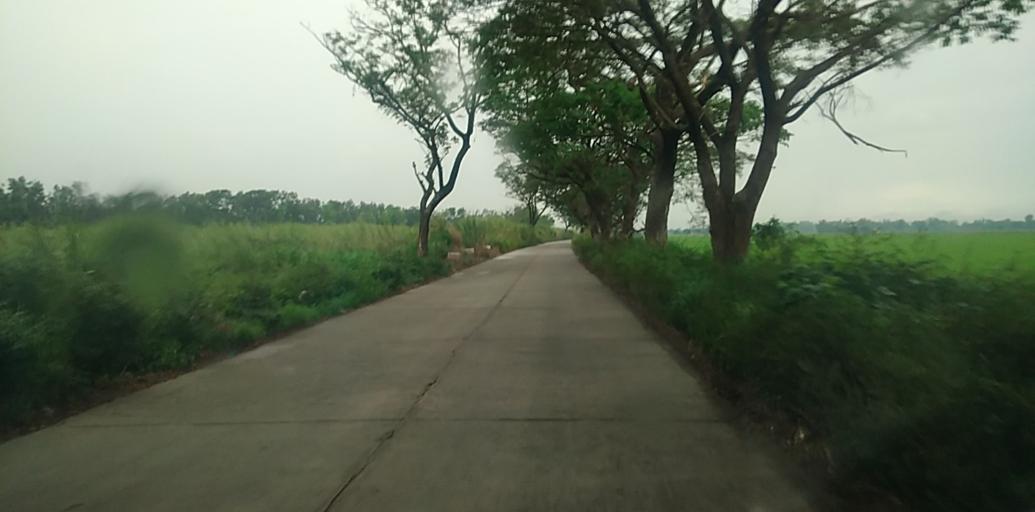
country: PH
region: Central Luzon
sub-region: Province of Pampanga
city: San Antonio
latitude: 15.1555
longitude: 120.6968
